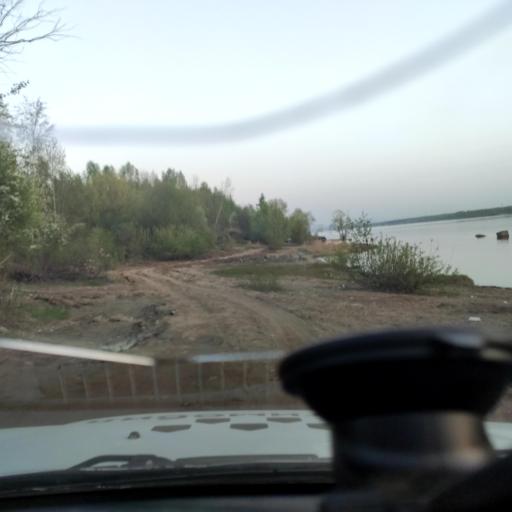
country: RU
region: Perm
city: Perm
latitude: 58.1115
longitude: 56.3391
